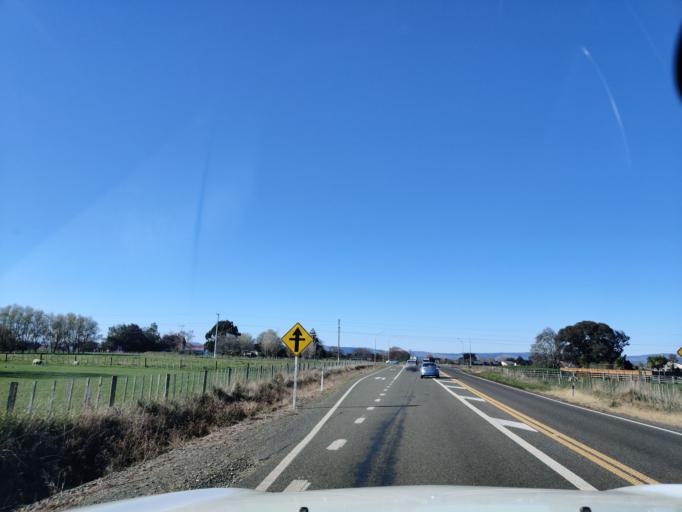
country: NZ
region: Manawatu-Wanganui
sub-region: Palmerston North City
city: Palmerston North
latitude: -40.3080
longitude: 175.5878
